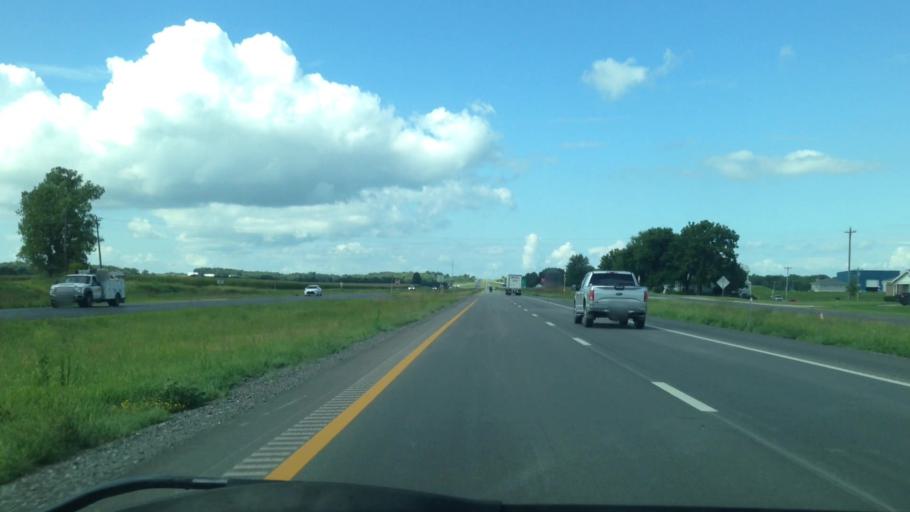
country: US
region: Illinois
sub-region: Adams County
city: Quincy
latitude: 39.9890
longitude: -91.5268
